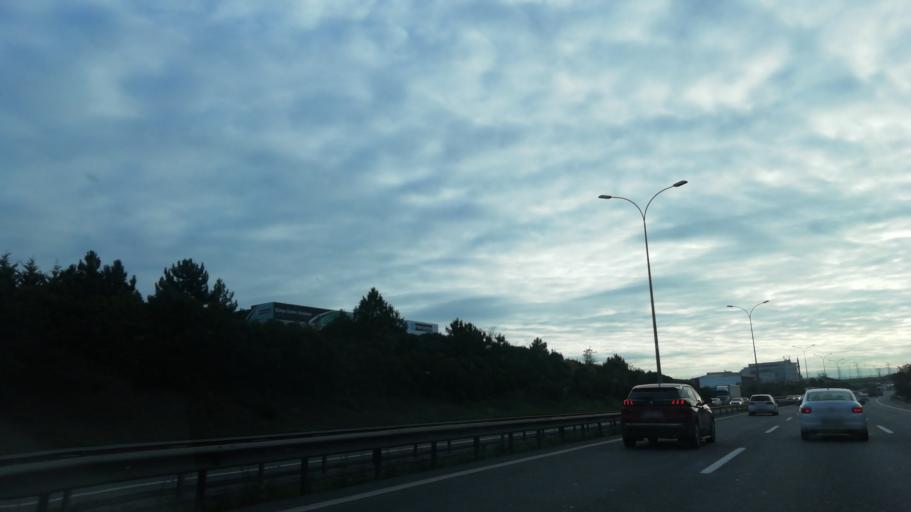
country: TR
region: Istanbul
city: Sultanbeyli
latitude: 40.9587
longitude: 29.2870
